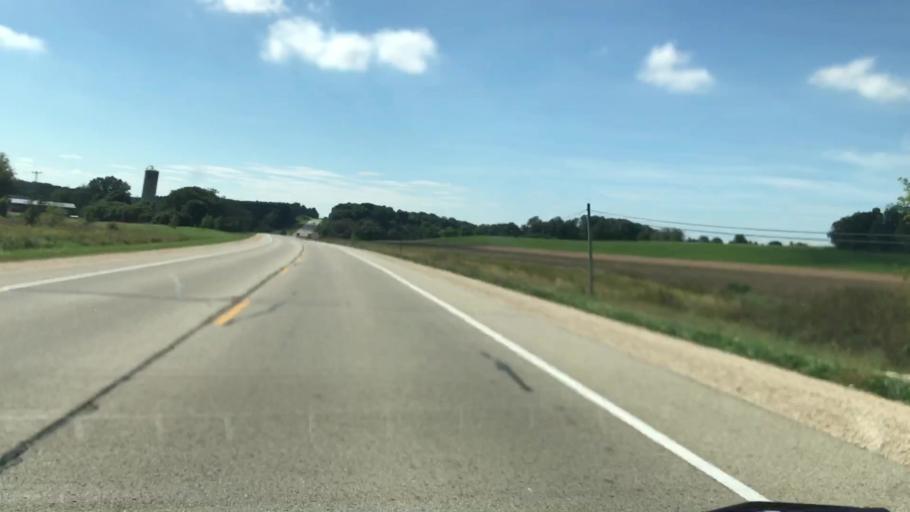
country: US
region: Wisconsin
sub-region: Dodge County
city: Mayville
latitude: 43.4851
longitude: -88.5839
